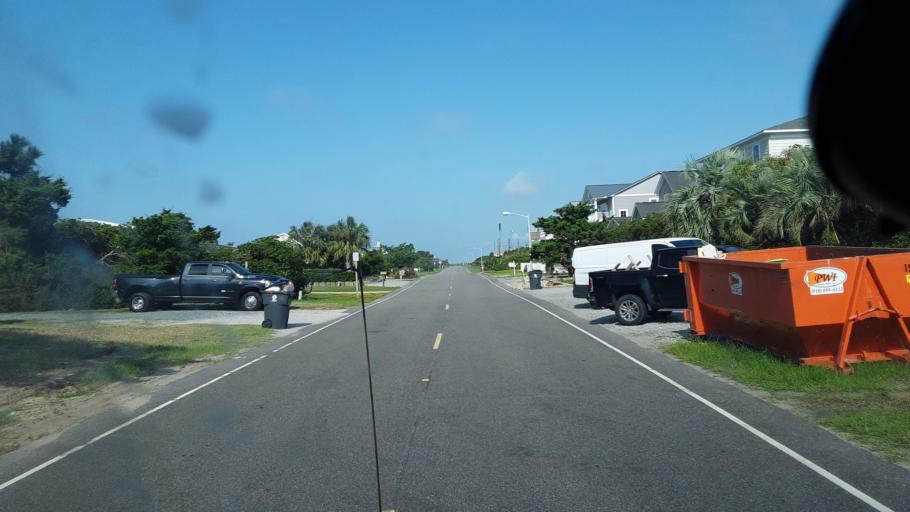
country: US
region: North Carolina
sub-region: Brunswick County
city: Southport
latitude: 33.8963
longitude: -78.0493
